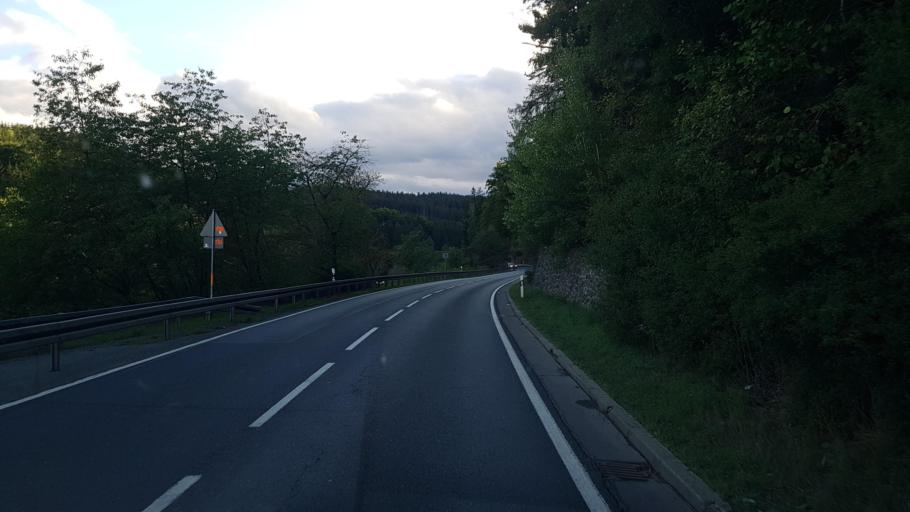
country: DE
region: Thuringia
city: Harra
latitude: 50.4492
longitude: 11.6906
